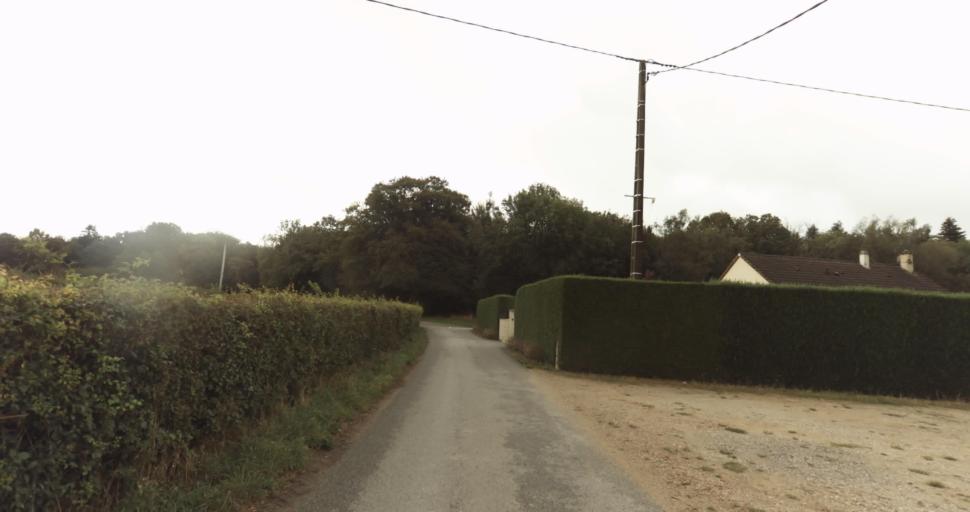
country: FR
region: Lower Normandy
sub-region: Departement de l'Orne
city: Gace
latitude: 48.8908
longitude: 0.3107
